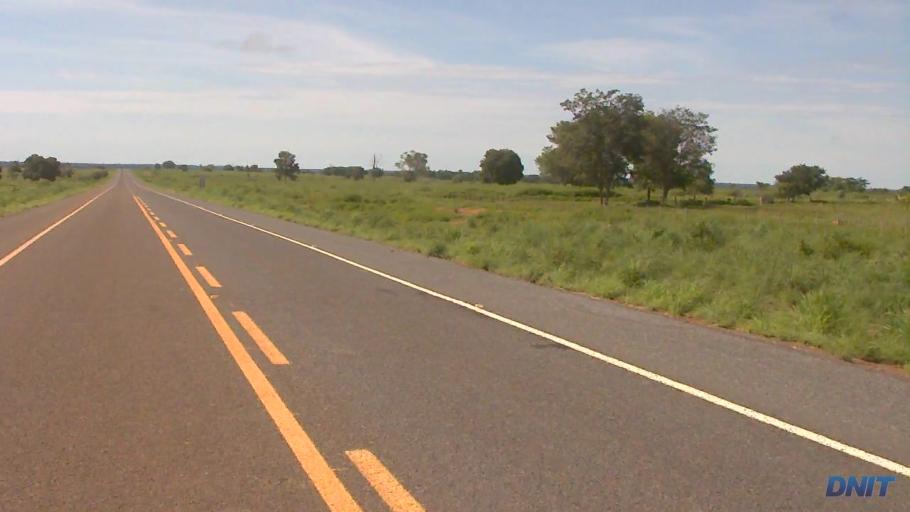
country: BR
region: Goias
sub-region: Sao Miguel Do Araguaia
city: Sao Miguel do Araguaia
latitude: -13.4691
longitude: -50.1153
